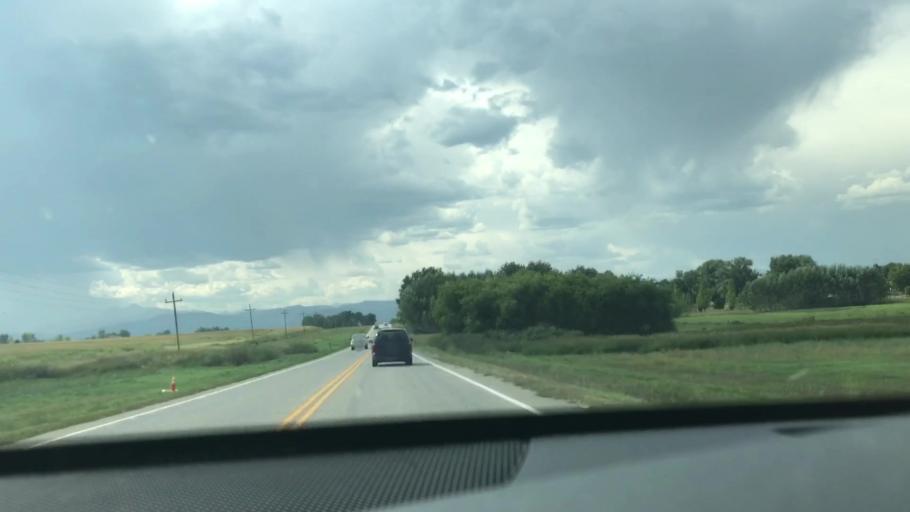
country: US
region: Colorado
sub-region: Larimer County
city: Loveland
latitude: 40.3794
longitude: -105.0032
